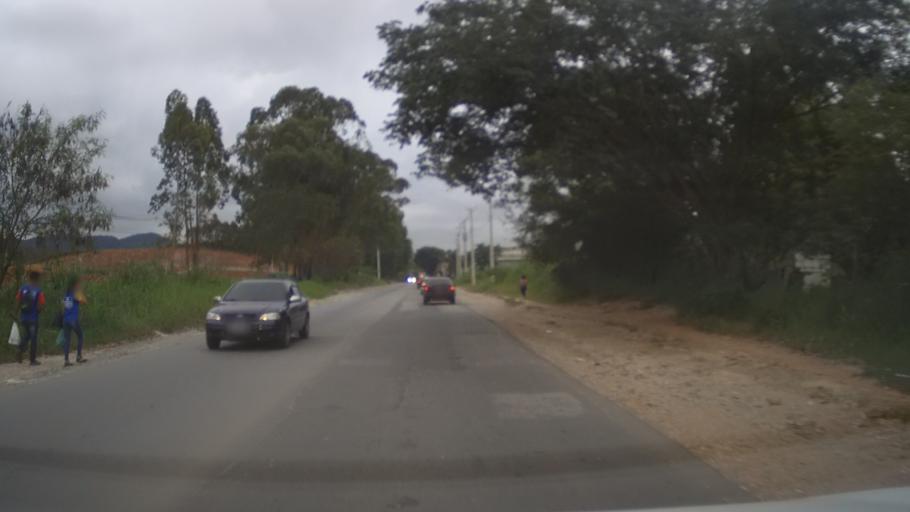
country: BR
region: Sao Paulo
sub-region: Guarulhos
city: Guarulhos
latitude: -23.3937
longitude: -46.4441
